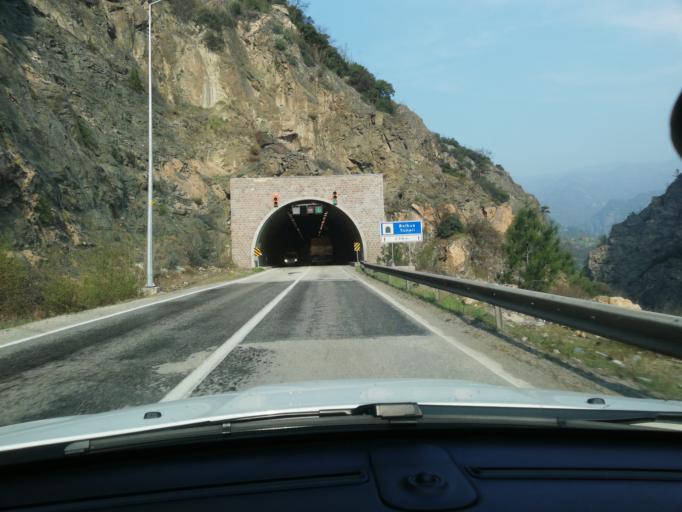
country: TR
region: Karabuk
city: Karabuk
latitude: 41.1533
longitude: 32.5226
